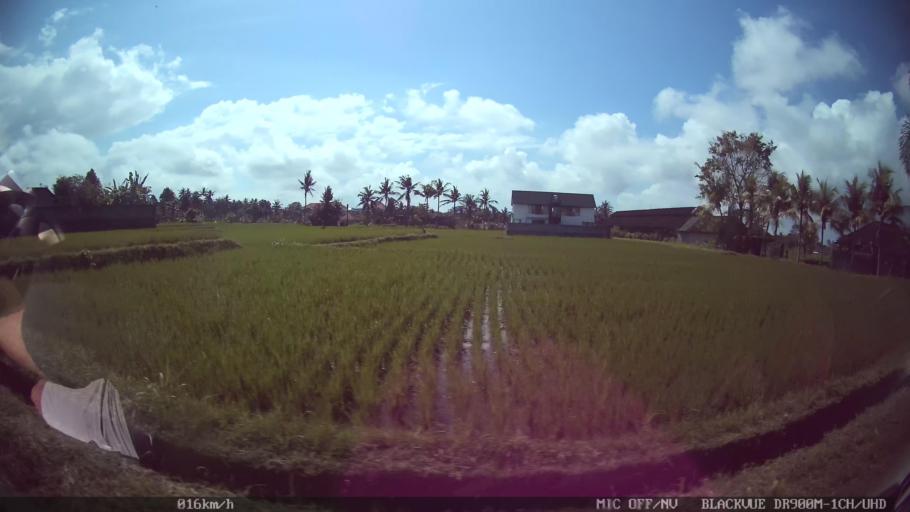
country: ID
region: Bali
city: Banjar Sedang
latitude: -8.5532
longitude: 115.2687
